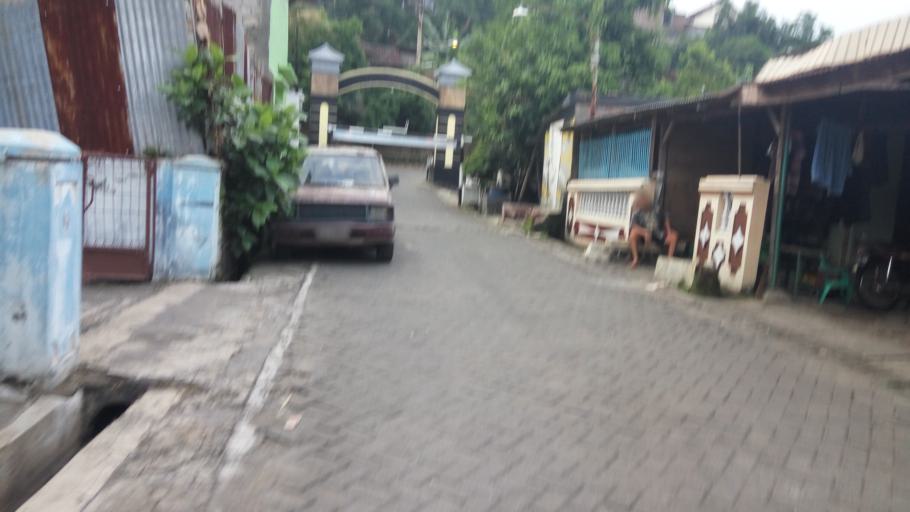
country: ID
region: Central Java
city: Semarang
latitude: -7.0165
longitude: 110.3846
